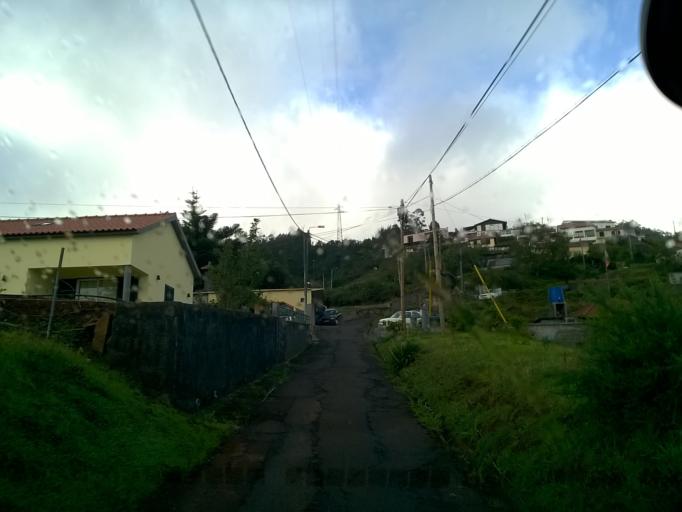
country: PT
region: Madeira
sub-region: Santa Cruz
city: Camacha
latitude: 32.6688
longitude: -16.8689
